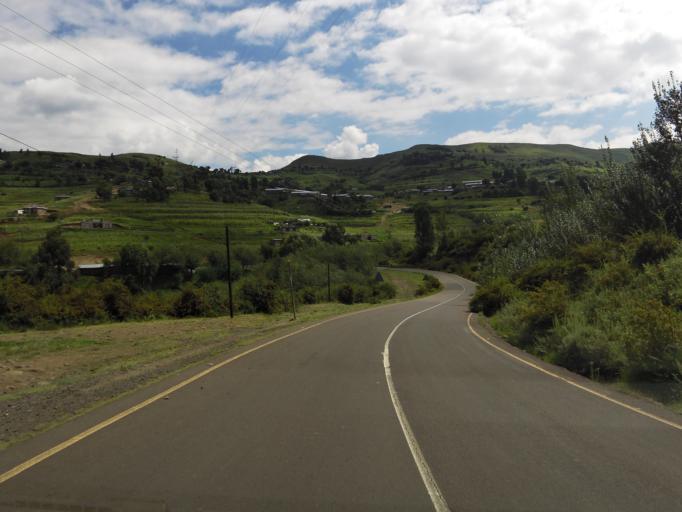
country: LS
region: Thaba-Tseka
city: Thaba-Tseka
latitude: -29.1418
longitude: 28.4878
